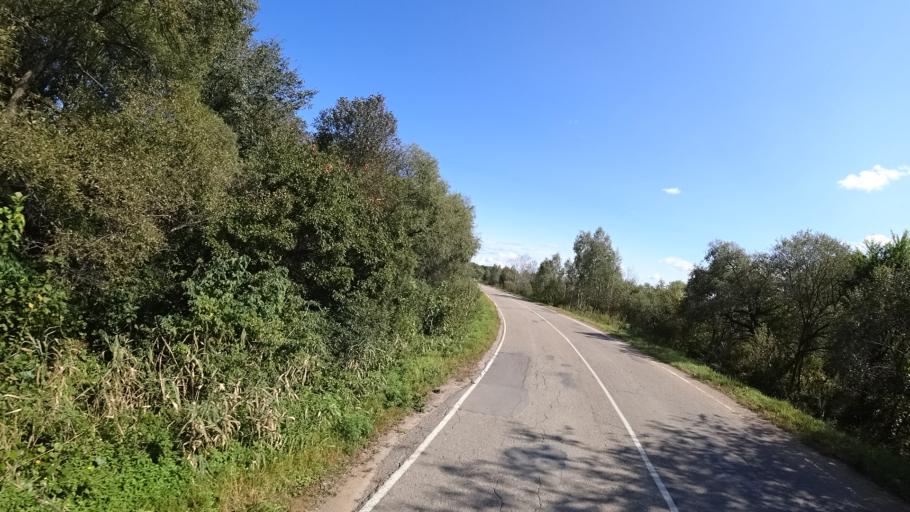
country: RU
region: Amur
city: Arkhara
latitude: 49.3998
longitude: 130.1322
